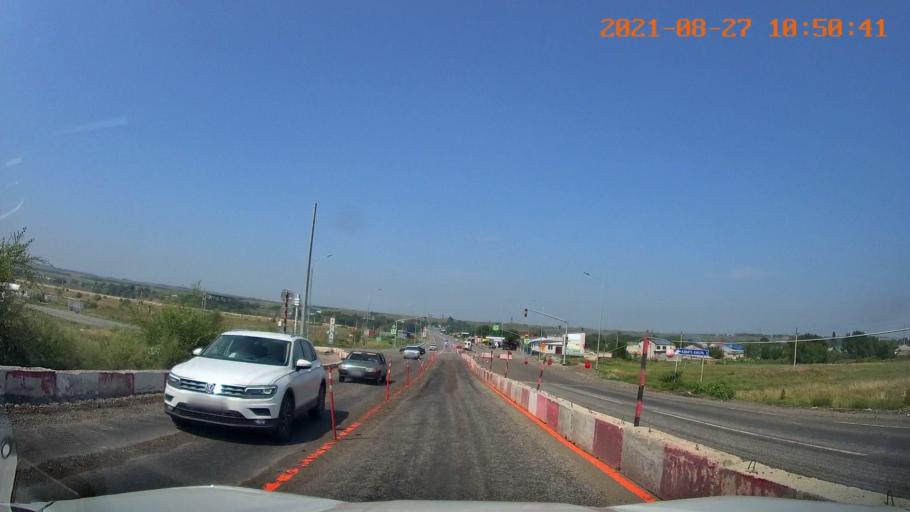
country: RU
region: Karachayevo-Cherkesiya
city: Adyge-Khabl'
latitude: 44.3604
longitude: 41.9433
